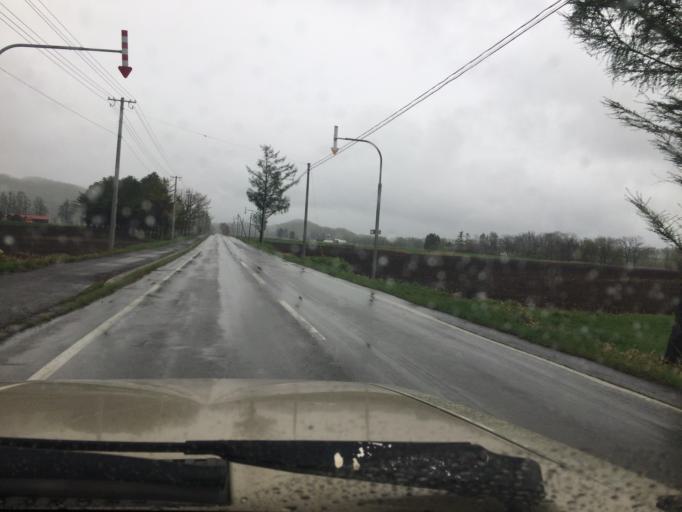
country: JP
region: Hokkaido
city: Obihiro
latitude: 42.8127
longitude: 142.9700
